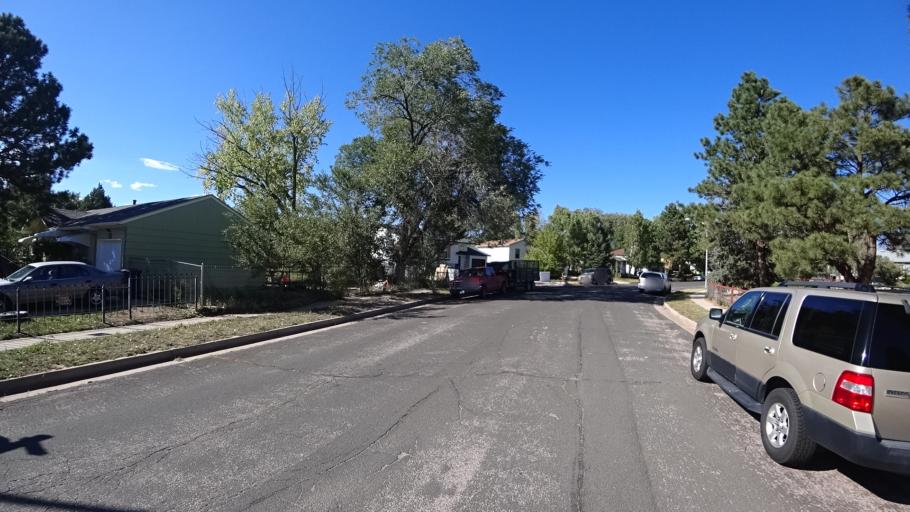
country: US
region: Colorado
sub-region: El Paso County
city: Stratmoor
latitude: 38.7943
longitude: -104.7539
